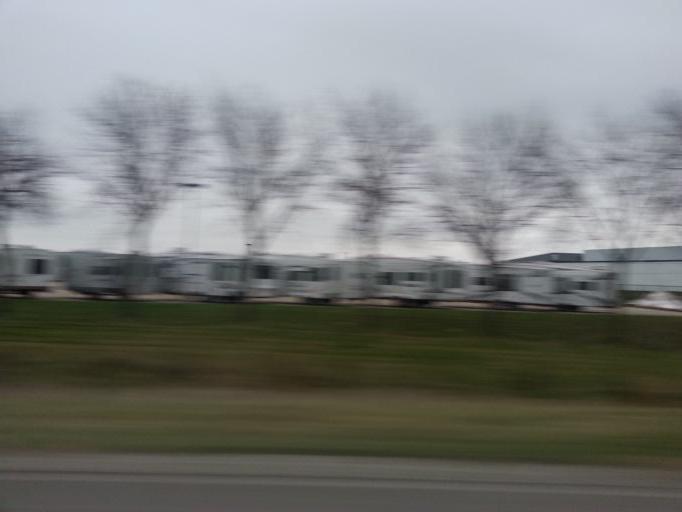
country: US
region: Iowa
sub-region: Linn County
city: Hiawatha
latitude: 42.0515
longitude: -91.6951
